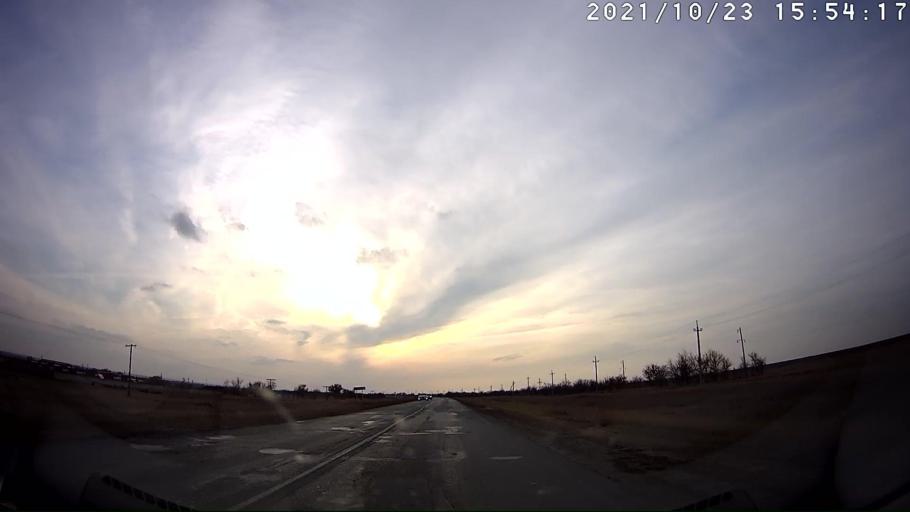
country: RU
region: Kalmykiya
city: Sadovoye
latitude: 47.9760
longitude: 43.9846
